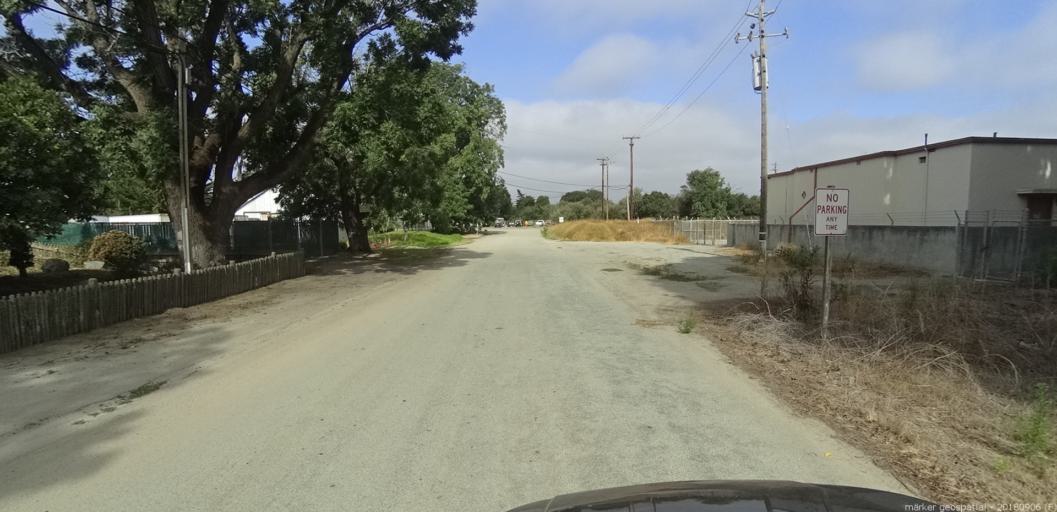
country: US
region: California
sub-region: Monterey County
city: Salinas
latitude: 36.6309
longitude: -121.6685
